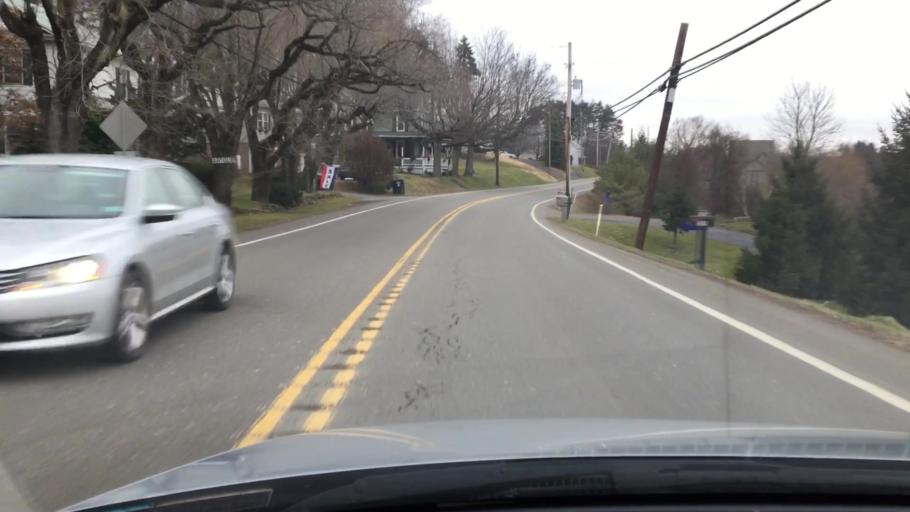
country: US
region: Pennsylvania
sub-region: Columbia County
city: Bloomsburg
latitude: 41.0175
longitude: -76.4374
